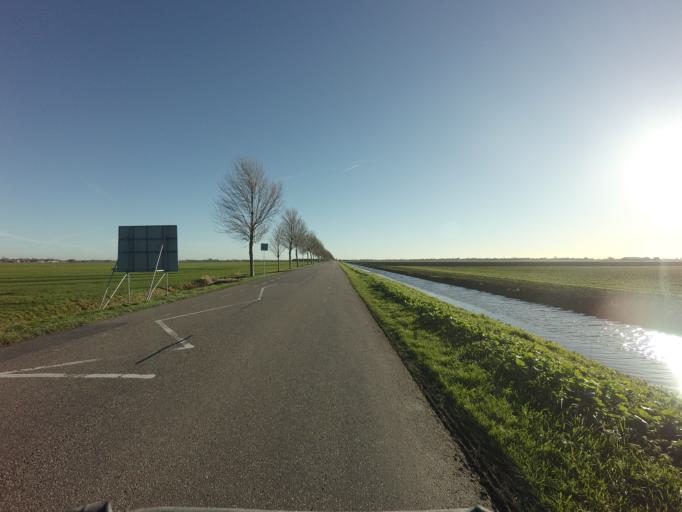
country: NL
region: South Holland
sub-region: Gemeente Nieuwkoop
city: Nieuwkoop
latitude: 52.1999
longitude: 4.7844
